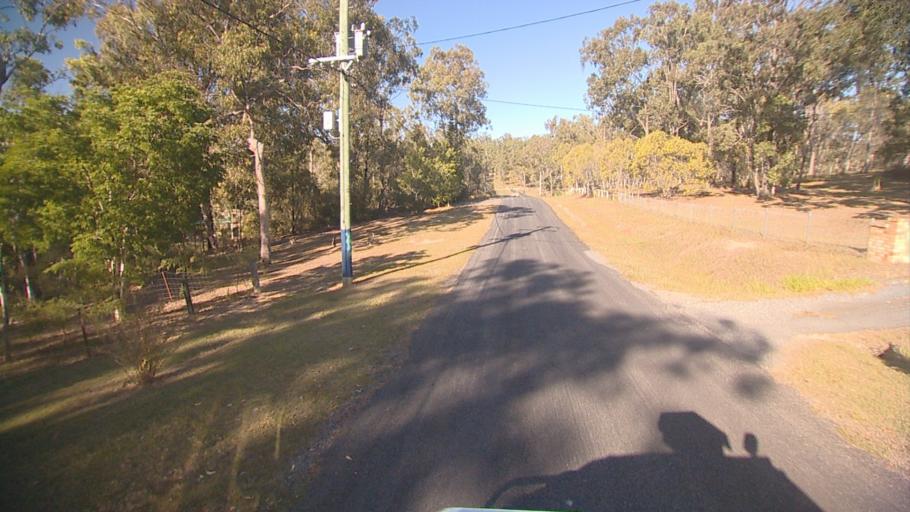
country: AU
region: Queensland
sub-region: Ipswich
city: Springfield Lakes
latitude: -27.6940
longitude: 152.9281
